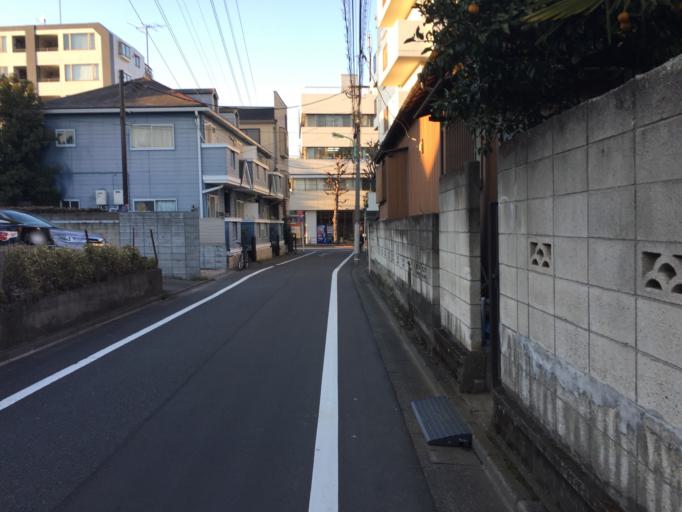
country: JP
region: Tokyo
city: Tokyo
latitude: 35.6498
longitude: 139.6644
